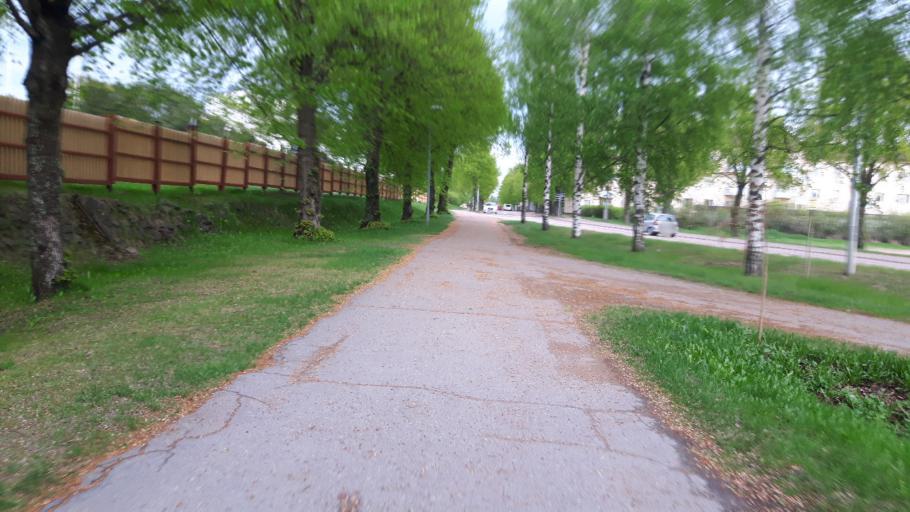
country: FI
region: Kymenlaakso
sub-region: Kotka-Hamina
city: Hamina
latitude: 60.5647
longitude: 27.1994
